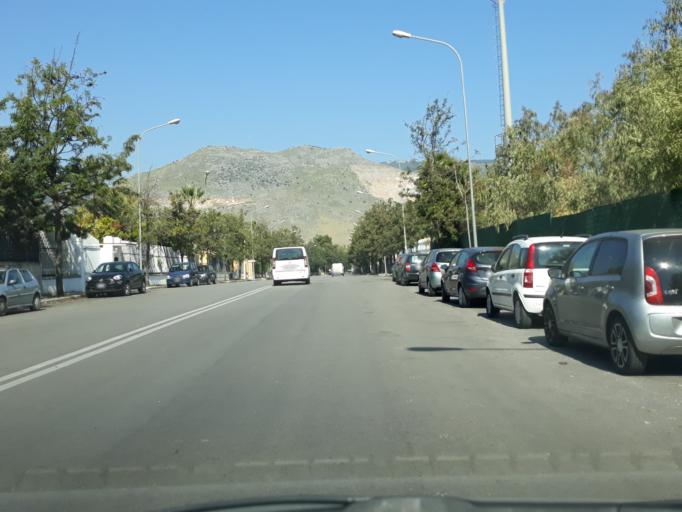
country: IT
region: Sicily
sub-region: Palermo
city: Palermo
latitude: 38.1221
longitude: 13.3048
